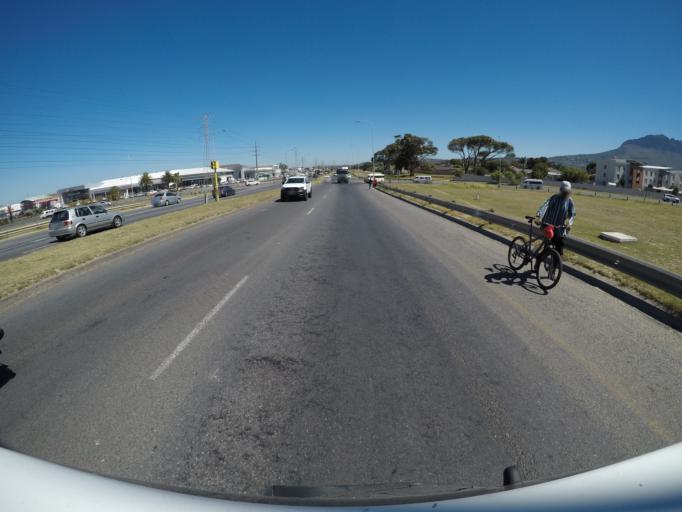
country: ZA
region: Western Cape
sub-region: Cape Winelands District Municipality
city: Stellenbosch
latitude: -34.0992
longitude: 18.8500
